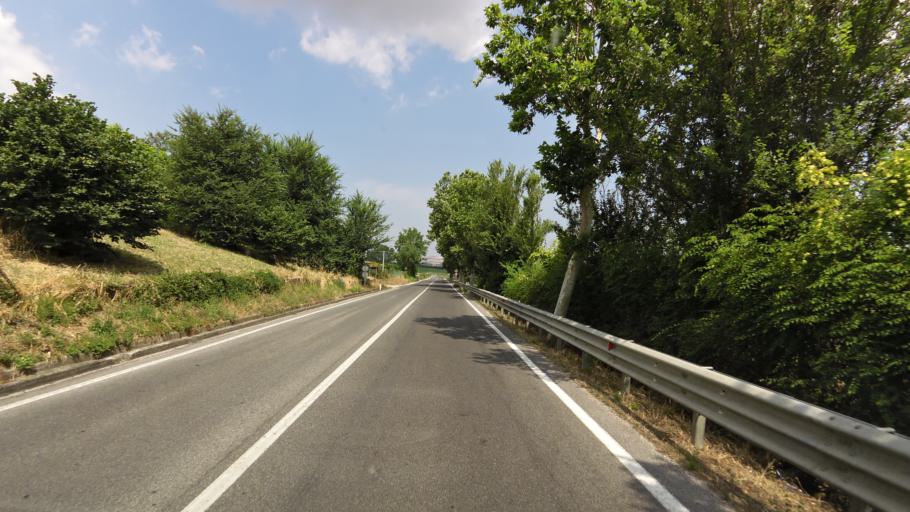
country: IT
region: The Marches
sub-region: Provincia di Ancona
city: Castelfidardo
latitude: 43.4790
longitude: 13.5797
